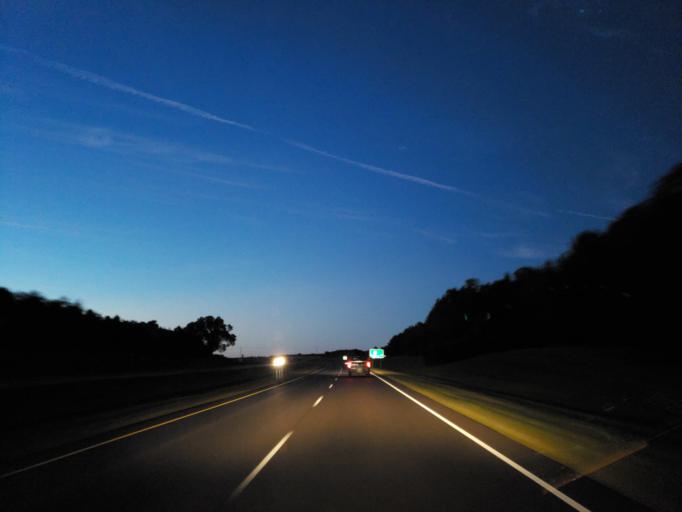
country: US
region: Mississippi
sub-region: Clarke County
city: Quitman
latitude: 32.0525
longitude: -88.6766
